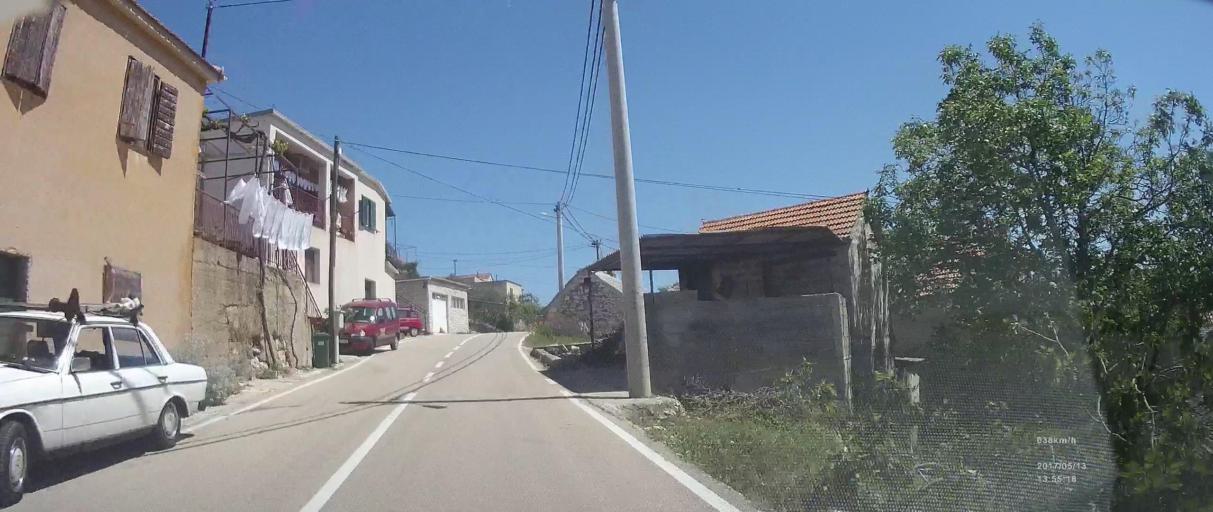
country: HR
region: Sibensko-Kniniska
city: Rogoznica
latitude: 43.5952
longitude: 16.0139
